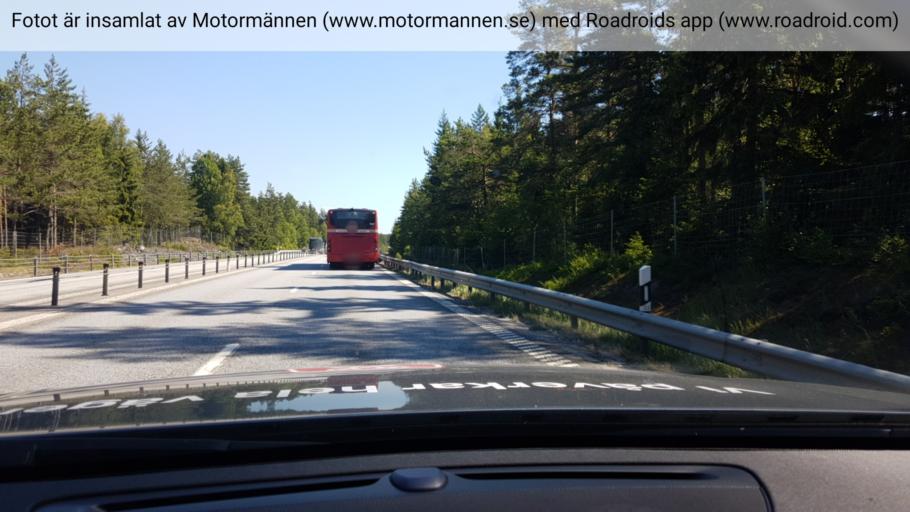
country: SE
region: Stockholm
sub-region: Osterakers Kommun
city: Akersberga
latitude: 59.6153
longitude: 18.2907
